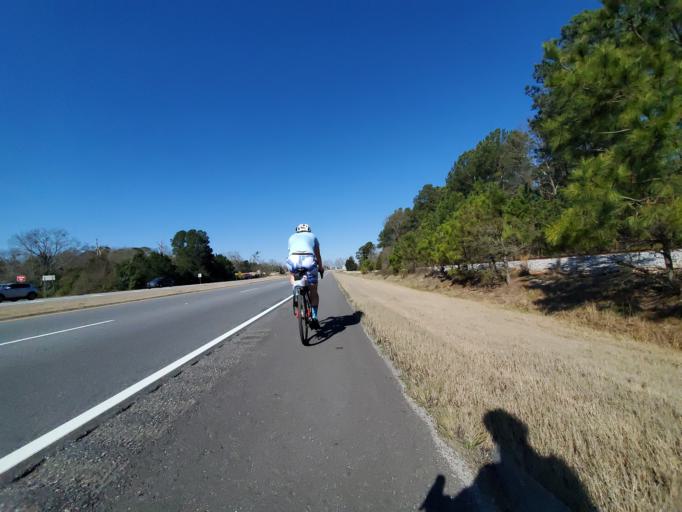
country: US
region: Georgia
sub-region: Clarke County
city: Country Club Estates
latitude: 34.0045
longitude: -83.4523
